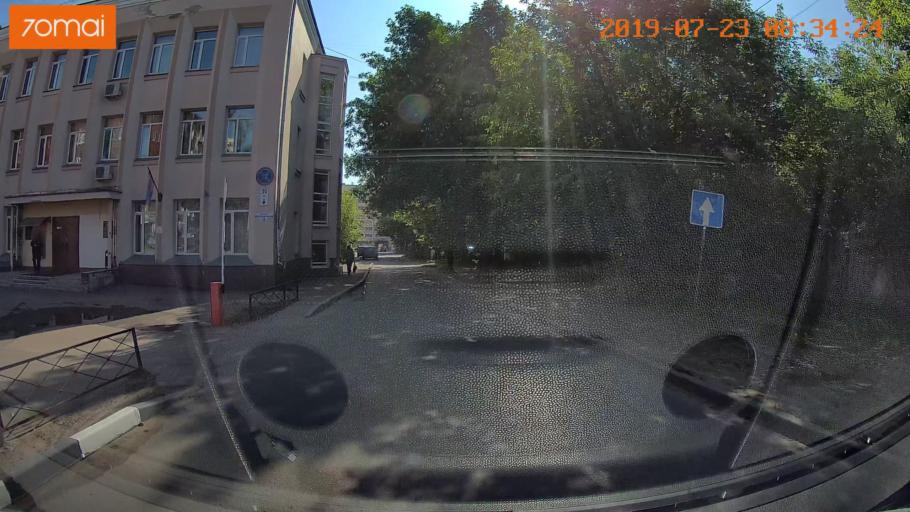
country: RU
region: Ivanovo
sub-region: Gorod Ivanovo
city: Ivanovo
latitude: 57.0047
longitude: 40.9773
